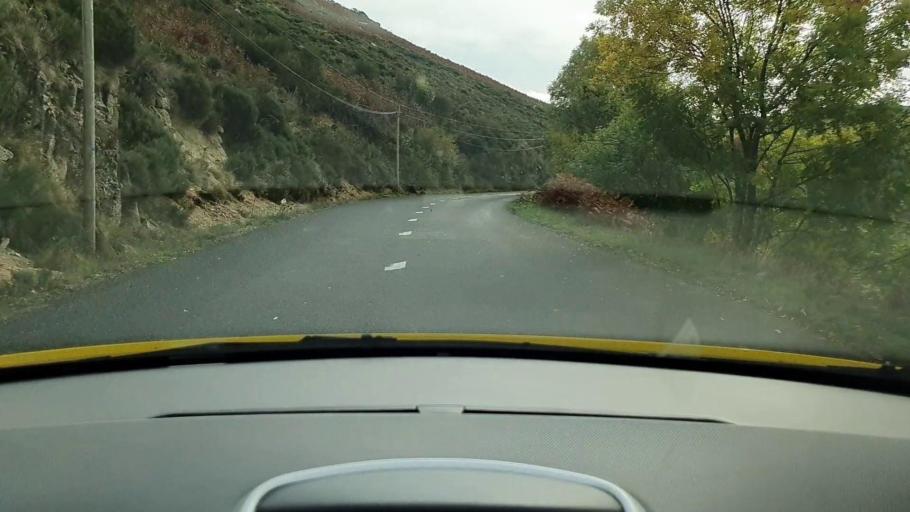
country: FR
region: Languedoc-Roussillon
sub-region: Departement de la Lozere
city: Meyrueis
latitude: 44.0760
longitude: 3.4754
